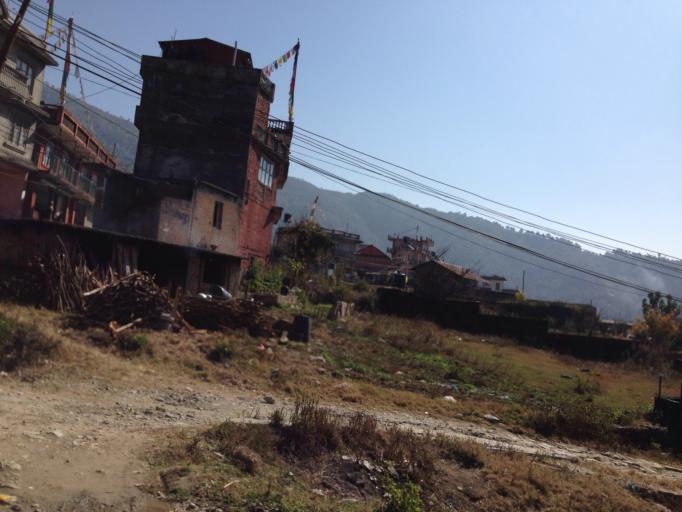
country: NP
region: Central Region
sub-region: Bagmati Zone
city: Kathmandu
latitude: 27.7786
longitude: 85.3669
